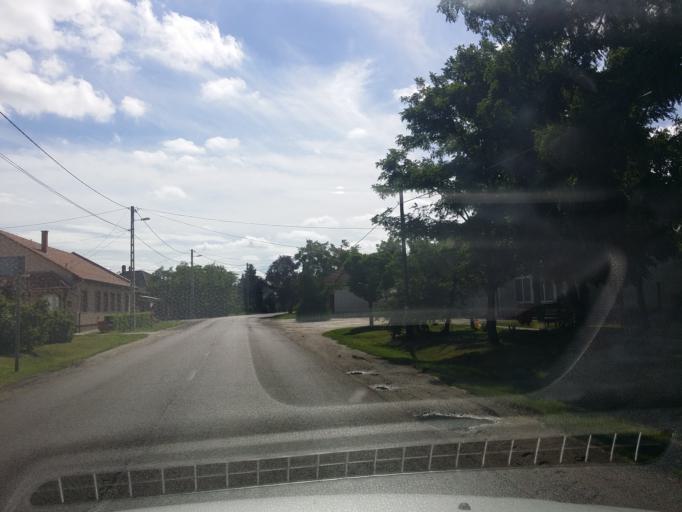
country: HU
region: Jasz-Nagykun-Szolnok
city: Jaszszentandras
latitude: 47.6429
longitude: 20.1886
